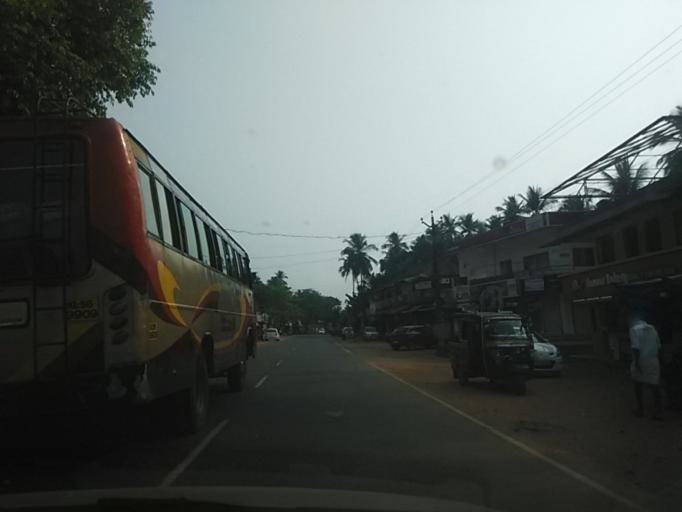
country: IN
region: Kerala
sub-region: Kozhikode
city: Naduvannur
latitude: 11.4849
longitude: 75.7751
